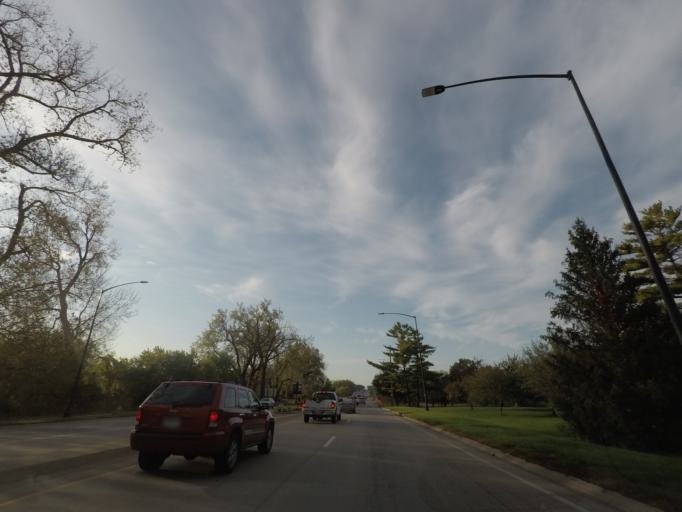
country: US
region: Iowa
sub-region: Polk County
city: Des Moines
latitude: 41.5760
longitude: -93.6450
